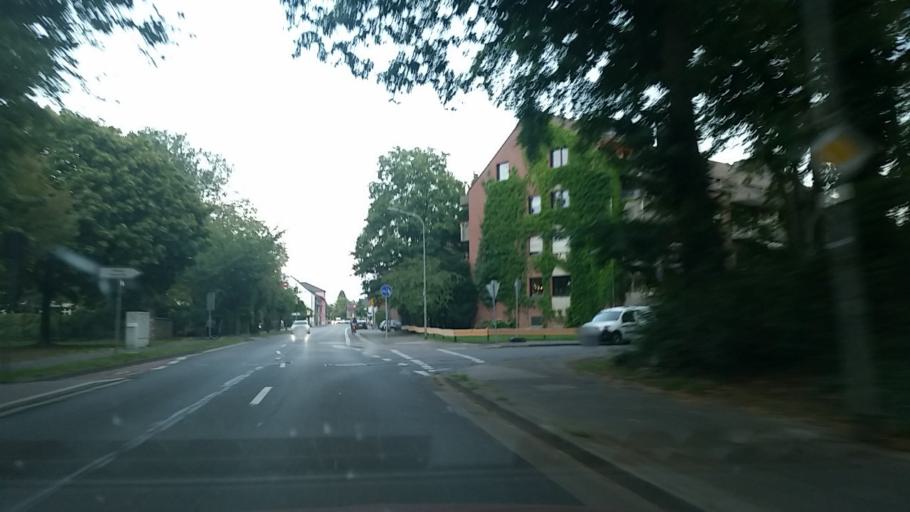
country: DE
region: North Rhine-Westphalia
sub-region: Regierungsbezirk Dusseldorf
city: Willich
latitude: 51.2666
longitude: 6.5495
